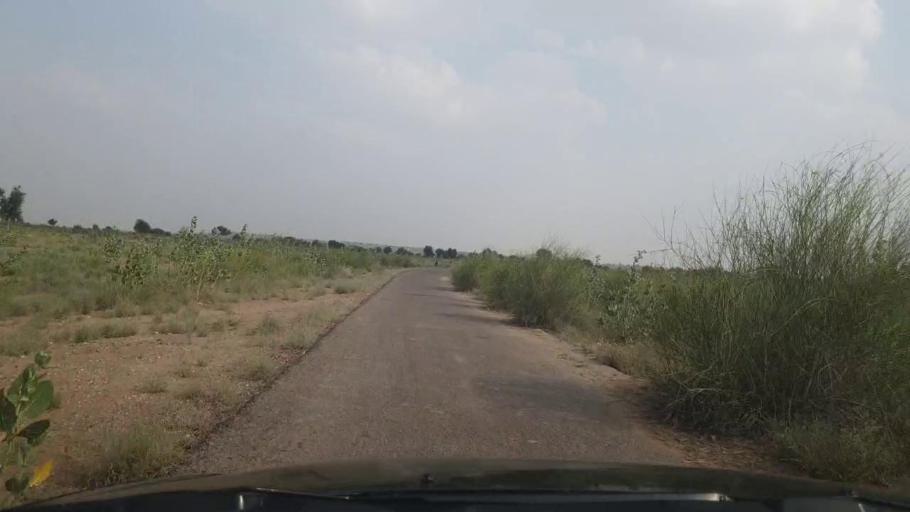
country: PK
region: Sindh
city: Islamkot
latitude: 25.0125
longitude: 70.5943
